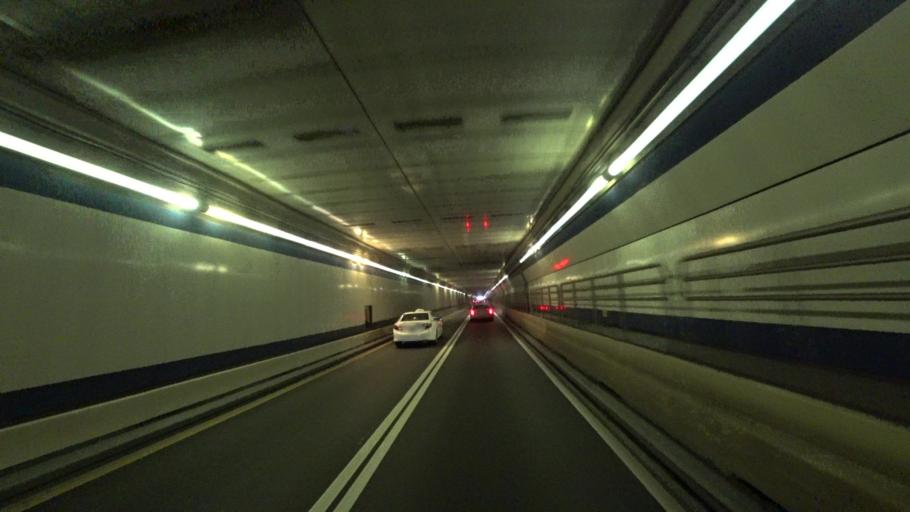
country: US
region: Massachusetts
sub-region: Suffolk County
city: Boston
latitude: 42.3687
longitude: -71.0448
